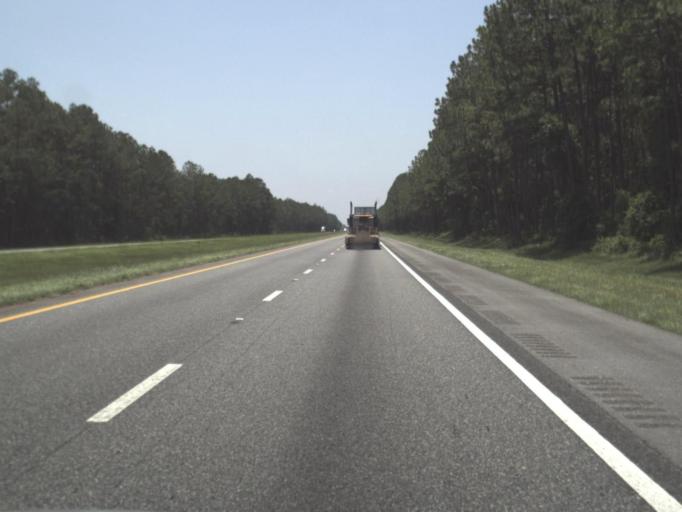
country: US
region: Florida
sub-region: Union County
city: Lake Butler
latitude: 30.2544
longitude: -82.3696
